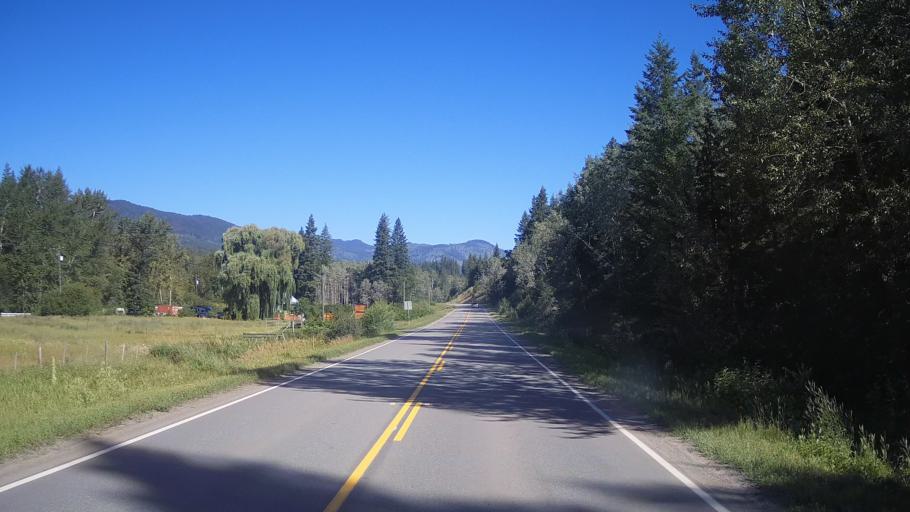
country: CA
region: British Columbia
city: Kamloops
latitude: 51.4375
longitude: -120.2090
